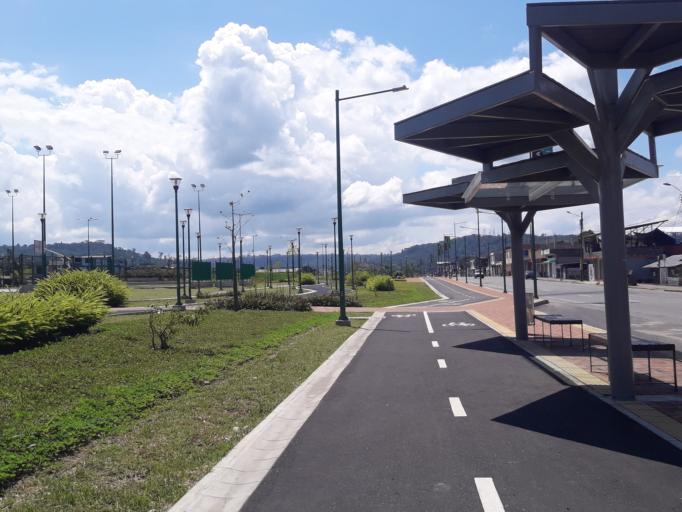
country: EC
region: Napo
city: Tena
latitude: -0.9861
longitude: -77.8236
